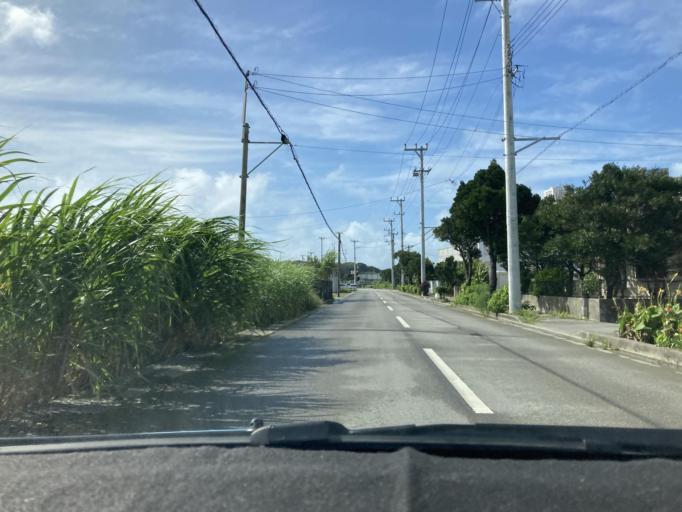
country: JP
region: Okinawa
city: Itoman
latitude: 26.1025
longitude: 127.6620
